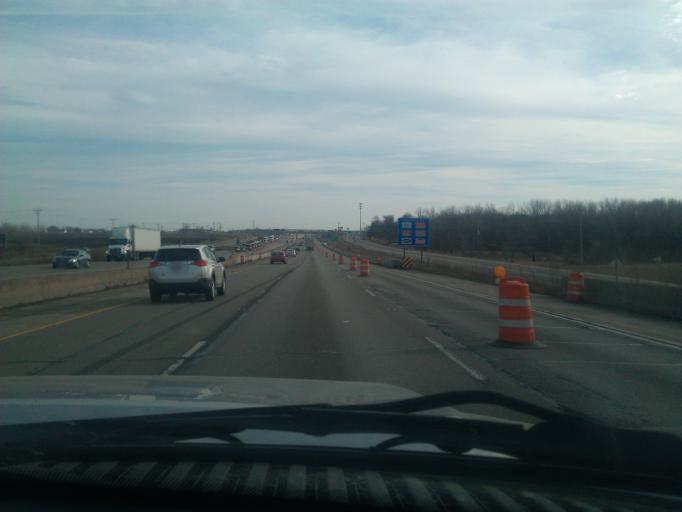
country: US
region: Wisconsin
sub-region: Racine County
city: Franksville
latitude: 42.7407
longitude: -87.9542
